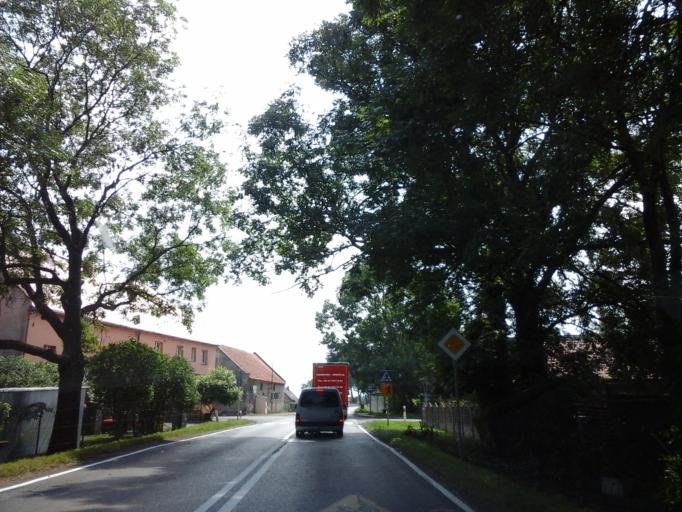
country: PL
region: Lower Silesian Voivodeship
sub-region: Powiat wroclawski
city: Zorawina
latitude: 50.9419
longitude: 17.0705
